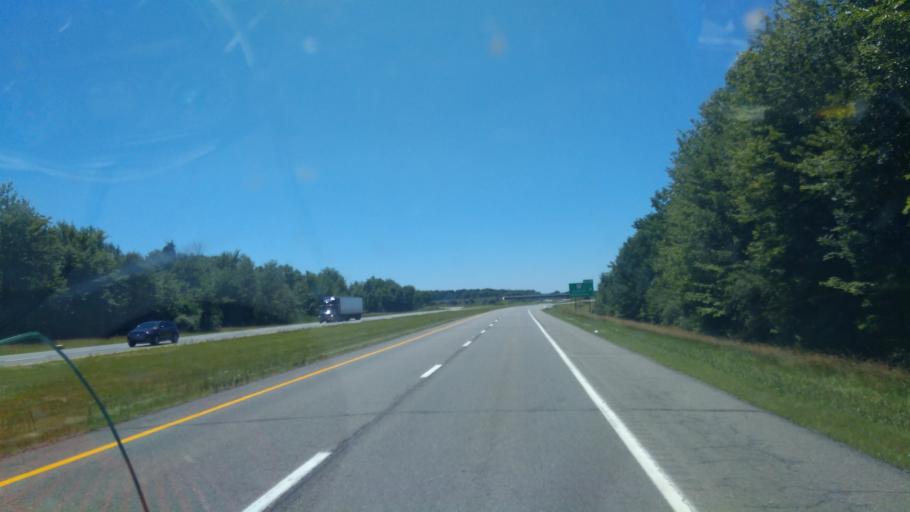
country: US
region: Ohio
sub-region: Trumbull County
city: Cortland
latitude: 41.4683
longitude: -80.7123
